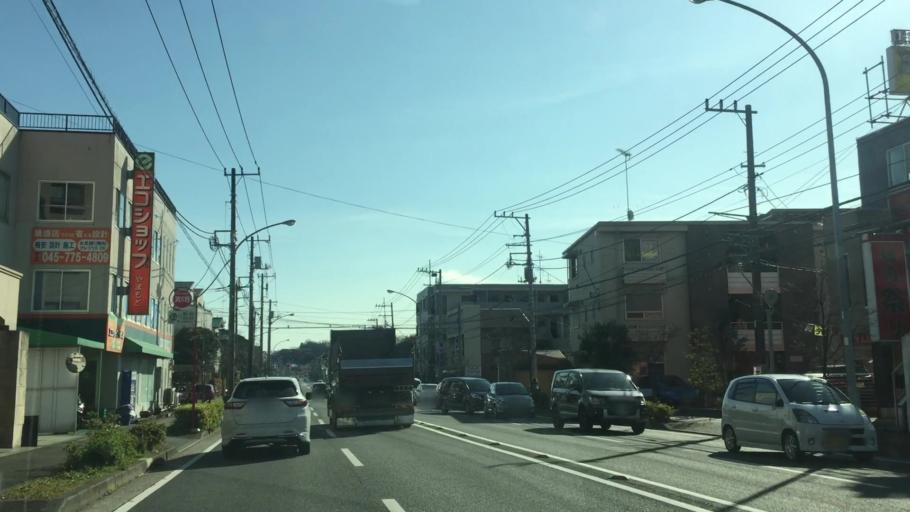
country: JP
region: Kanagawa
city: Yokohama
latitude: 35.3754
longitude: 139.6103
